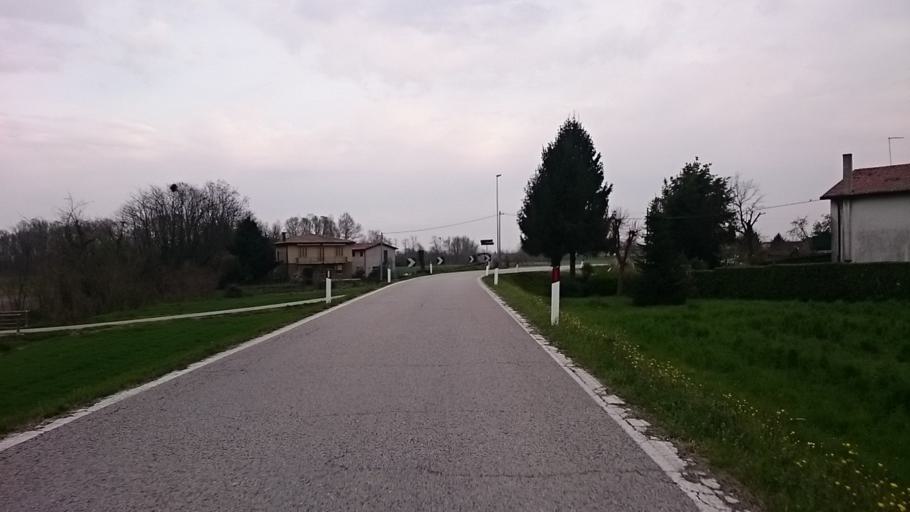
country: IT
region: Veneto
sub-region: Provincia di Padova
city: Tremignon
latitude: 45.5219
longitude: 11.8131
